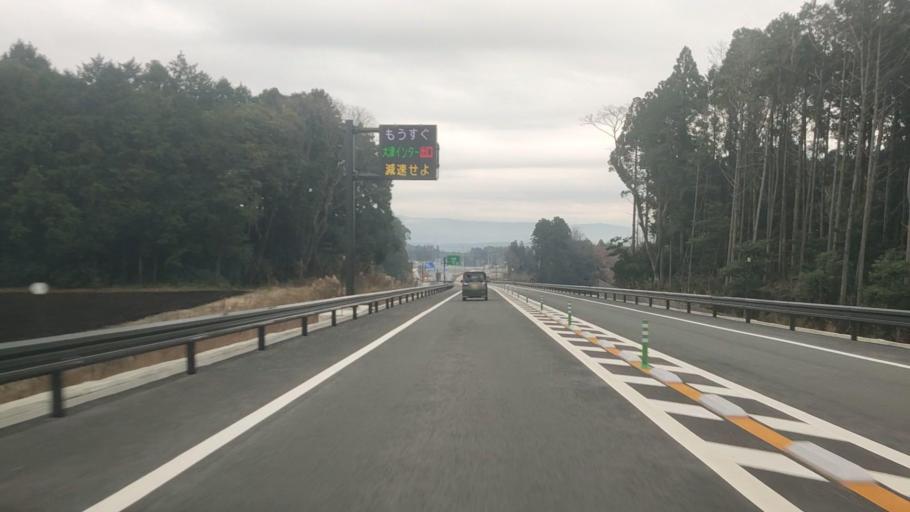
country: JP
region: Kumamoto
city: Ozu
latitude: 32.8947
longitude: 130.8960
